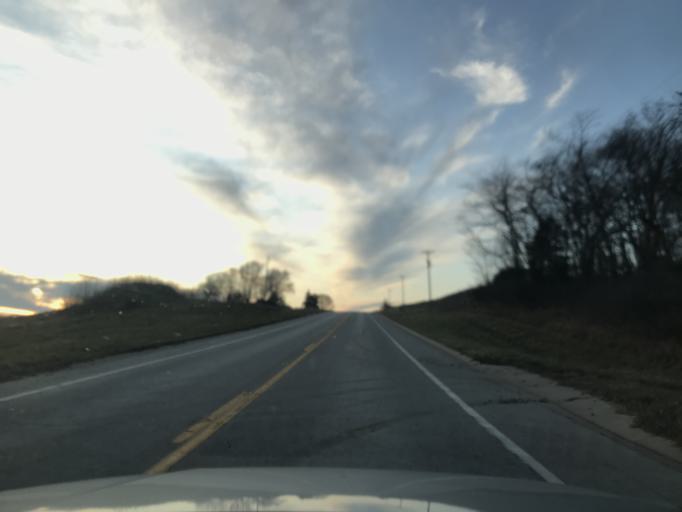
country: US
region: Illinois
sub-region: Henderson County
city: Oquawka
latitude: 41.0190
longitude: -90.8284
